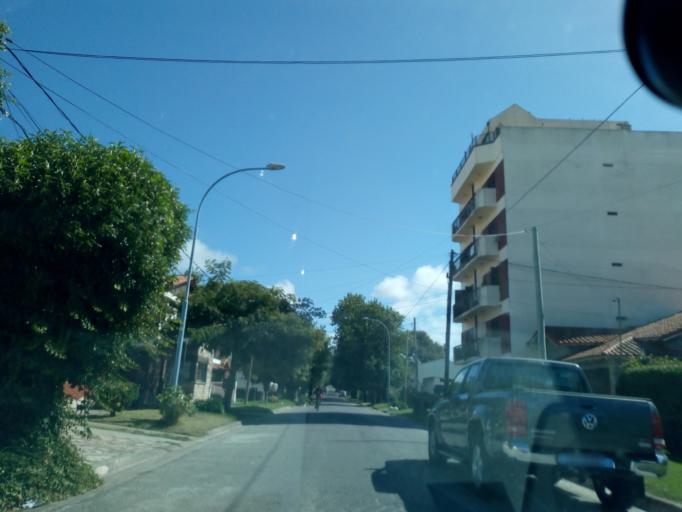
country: AR
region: Buenos Aires
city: Mar del Plata
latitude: -38.0677
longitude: -57.5481
